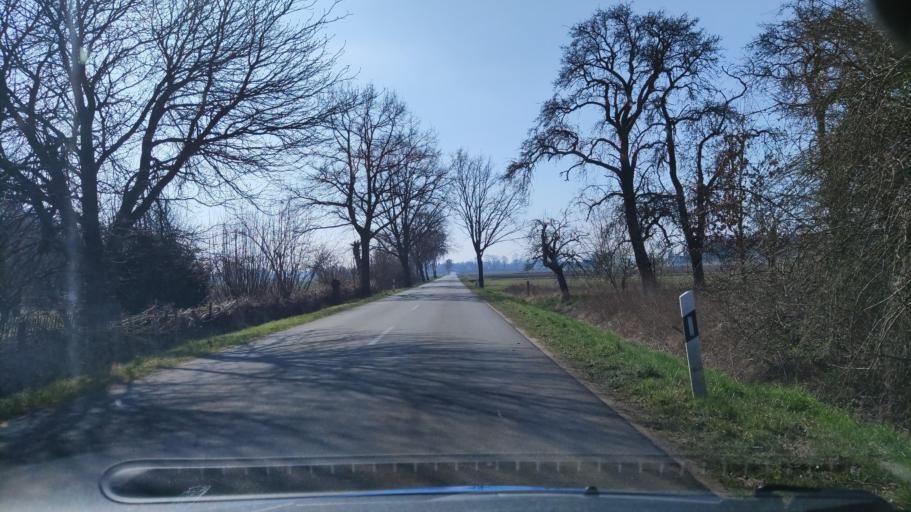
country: DE
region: Lower Saxony
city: Kusten
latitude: 52.9887
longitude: 11.0637
